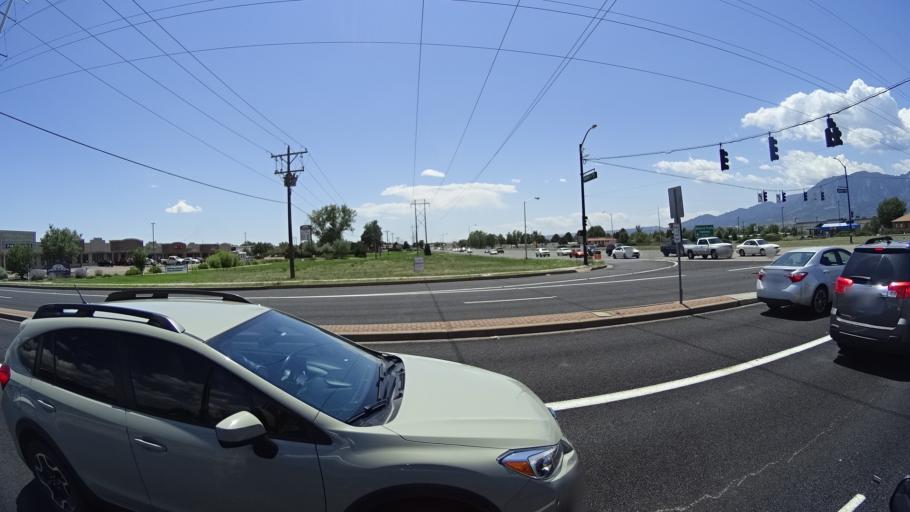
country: US
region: Colorado
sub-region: El Paso County
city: Stratmoor
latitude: 38.7892
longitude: -104.7571
